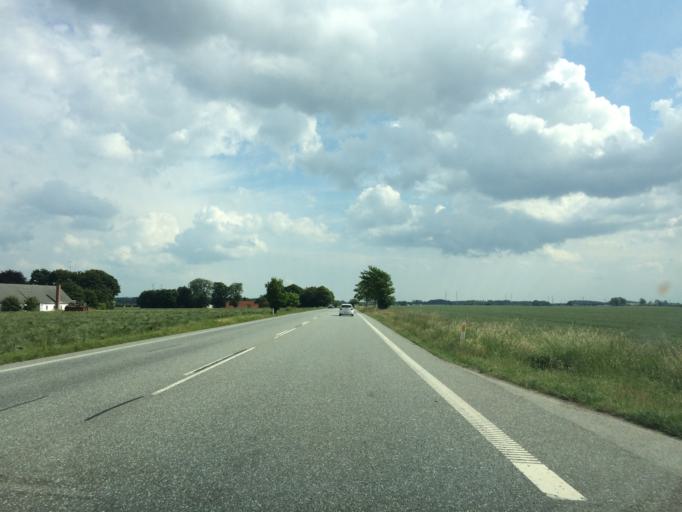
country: DK
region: South Denmark
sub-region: Fredericia Kommune
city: Taulov
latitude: 55.5755
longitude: 9.6629
